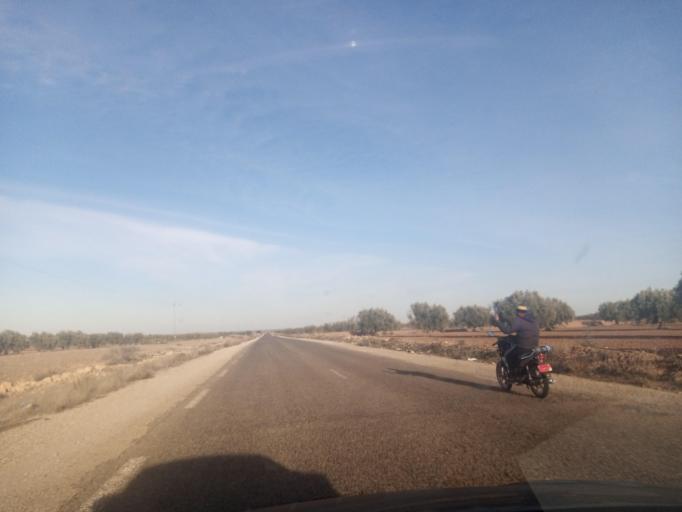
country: TN
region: Safaqis
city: Bi'r `Ali Bin Khalifah
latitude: 34.9322
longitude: 10.3279
